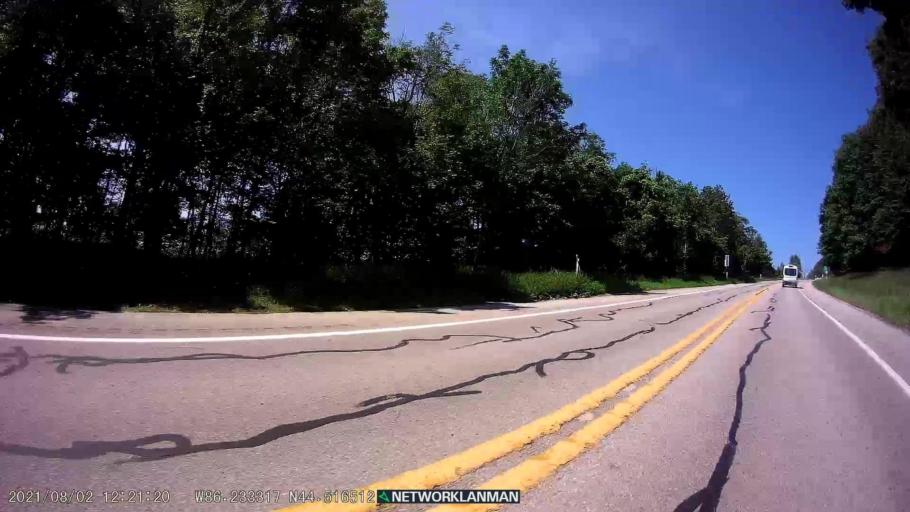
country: US
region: Michigan
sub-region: Benzie County
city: Frankfort
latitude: 44.5168
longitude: -86.2333
